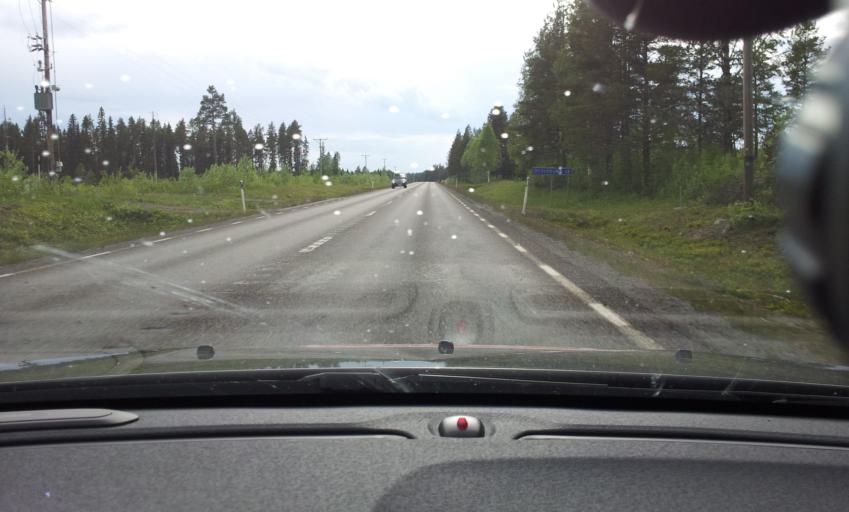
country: SE
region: Jaemtland
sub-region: OEstersunds Kommun
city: Lit
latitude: 63.2047
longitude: 14.8704
